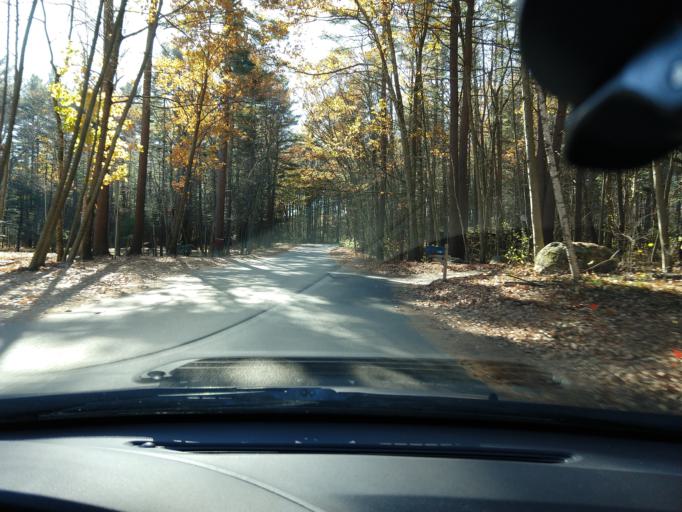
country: US
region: Massachusetts
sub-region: Middlesex County
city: Carlisle
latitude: 42.5092
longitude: -71.3293
